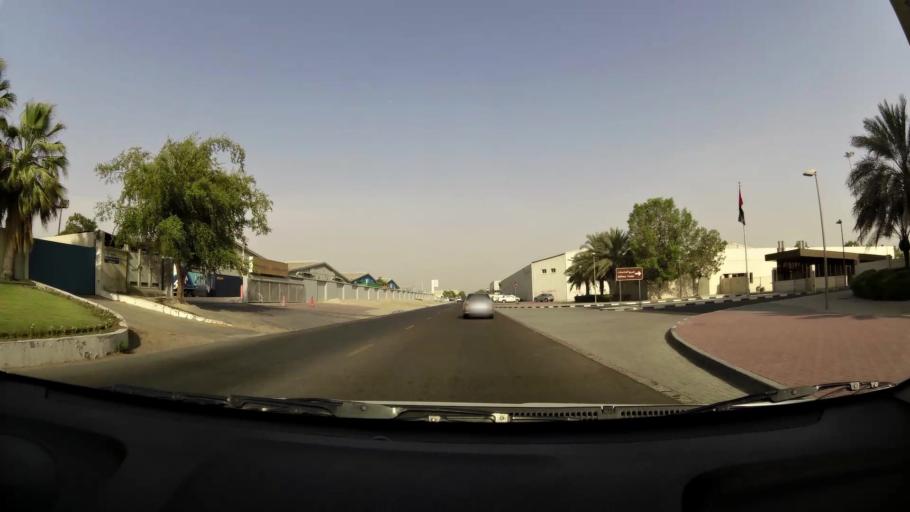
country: AE
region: Ash Shariqah
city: Sharjah
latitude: 25.2325
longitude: 55.3609
